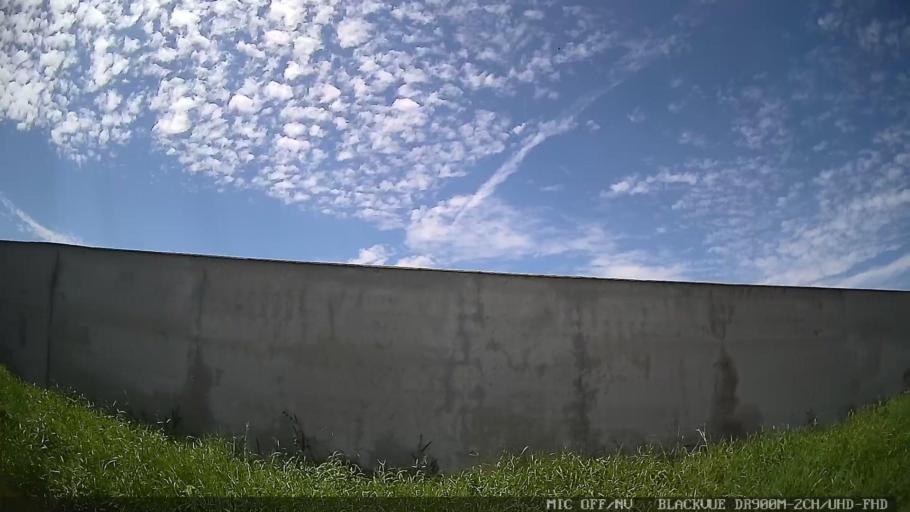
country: BR
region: Sao Paulo
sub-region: Iguape
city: Iguape
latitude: -24.7271
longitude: -47.5169
